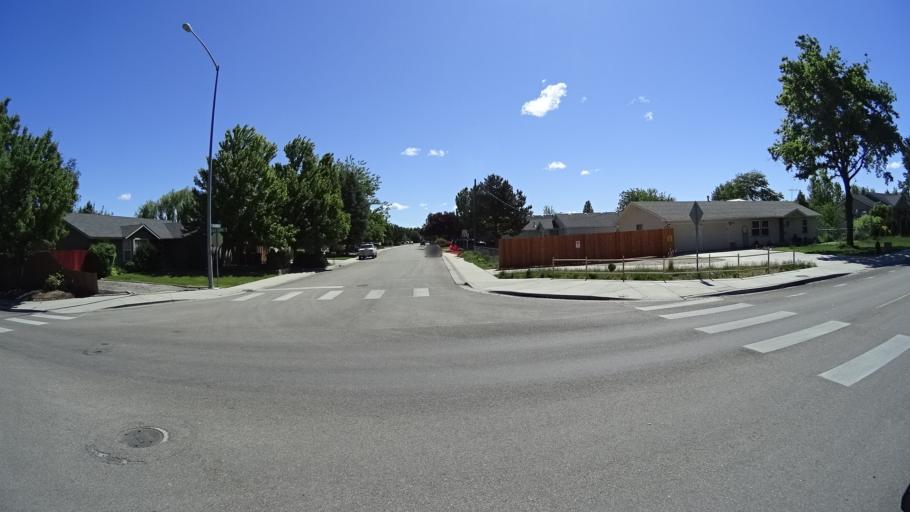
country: US
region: Idaho
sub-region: Ada County
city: Meridian
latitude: 43.6282
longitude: -116.3746
